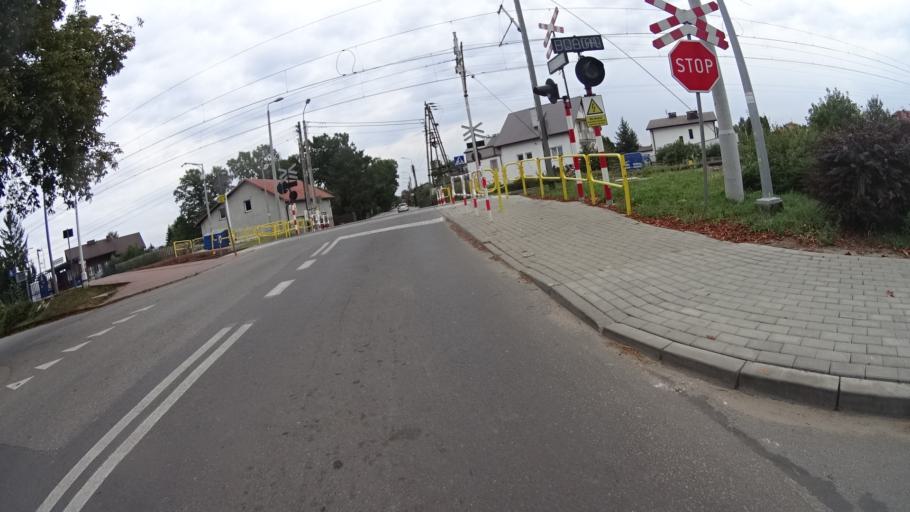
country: PL
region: Masovian Voivodeship
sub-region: Powiat pruszkowski
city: Granica
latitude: 52.1405
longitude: 20.7948
